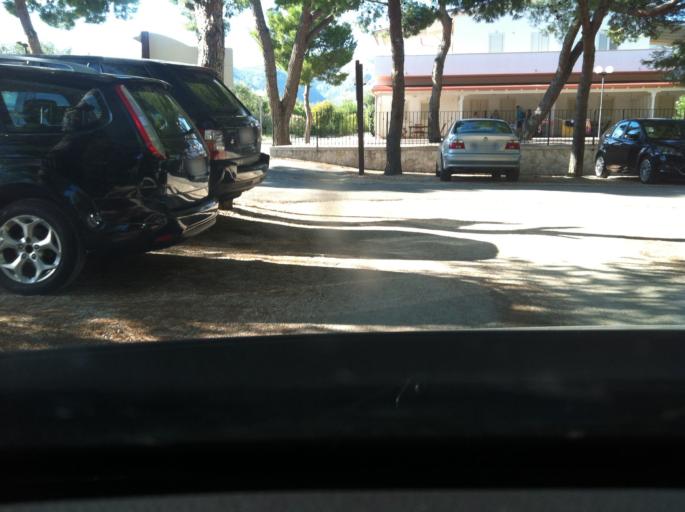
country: IT
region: Apulia
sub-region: Provincia di Foggia
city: Monte Sant'Angelo
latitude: 41.6559
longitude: 15.9766
